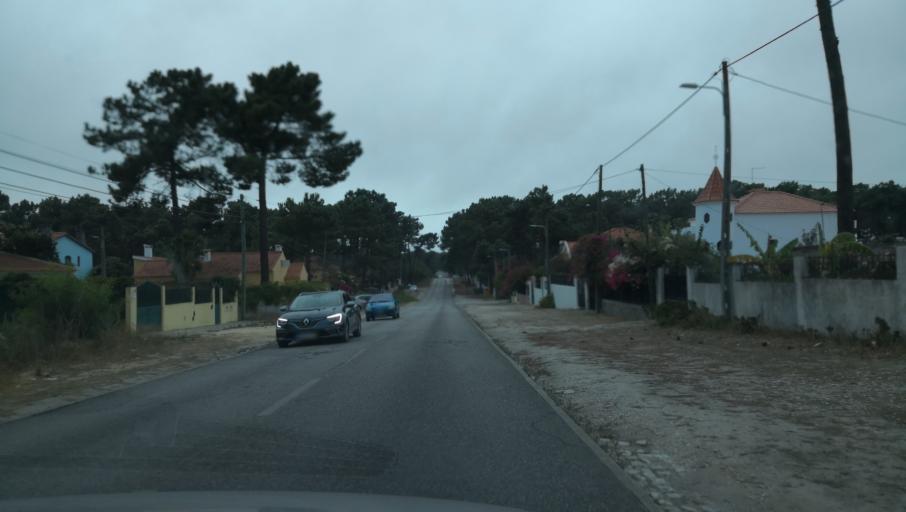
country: PT
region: Setubal
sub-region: Almada
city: Charneca
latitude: 38.5796
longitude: -9.1823
